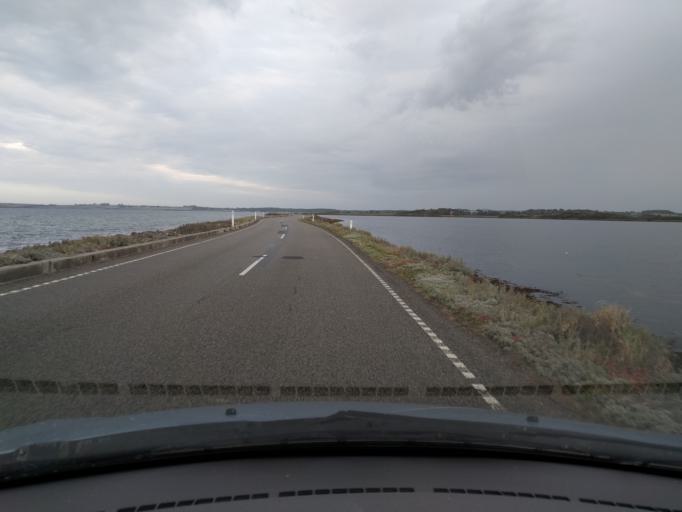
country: DK
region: South Denmark
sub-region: Assens Kommune
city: Assens
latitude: 55.1799
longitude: 9.9858
